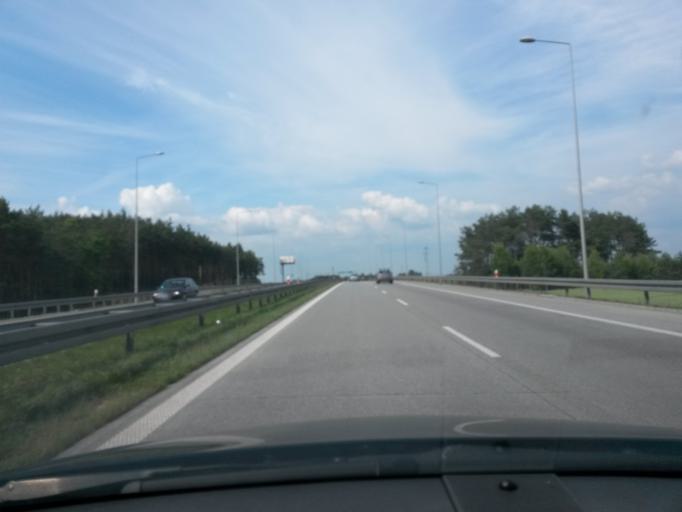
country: PL
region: Lodz Voivodeship
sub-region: Powiat rawski
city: Rawa Mazowiecka
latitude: 51.7002
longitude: 20.2181
